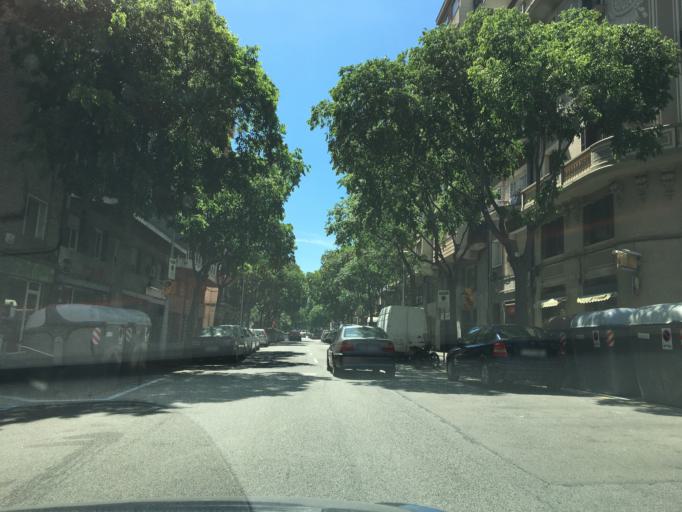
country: ES
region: Catalonia
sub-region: Provincia de Barcelona
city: Horta-Guinardo
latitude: 41.4112
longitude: 2.1789
